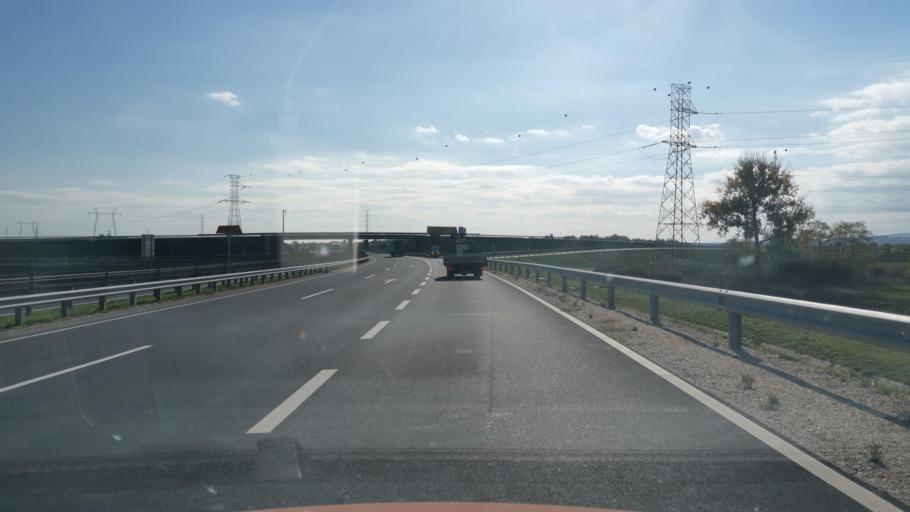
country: HU
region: Borsod-Abauj-Zemplen
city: Arnot
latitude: 48.1382
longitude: 20.8343
